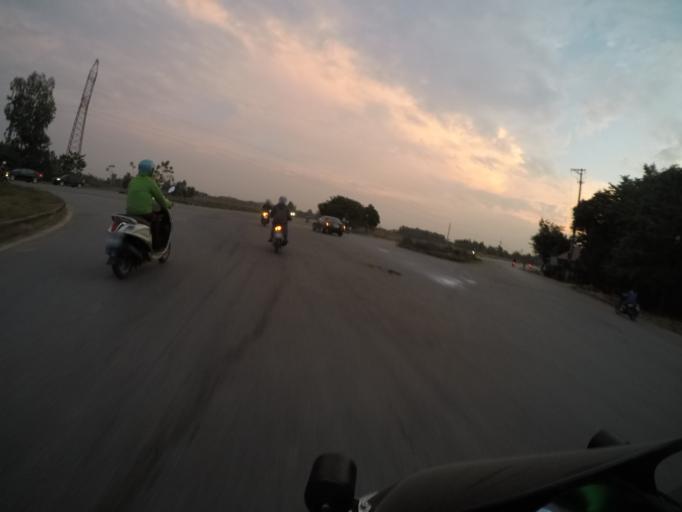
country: VN
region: Vinh Phuc
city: Phuc Yen
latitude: 21.2662
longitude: 105.7226
